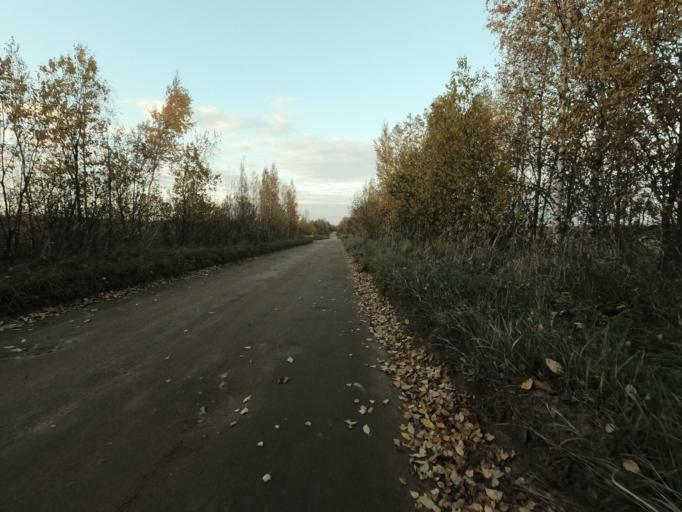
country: RU
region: Leningrad
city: Mga
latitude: 59.7980
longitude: 31.2001
